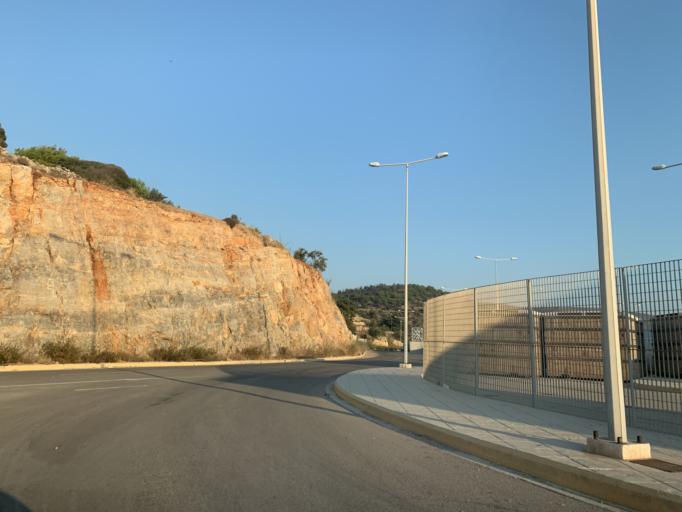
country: GR
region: North Aegean
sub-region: Chios
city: Thymiana
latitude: 38.2919
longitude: 25.9293
